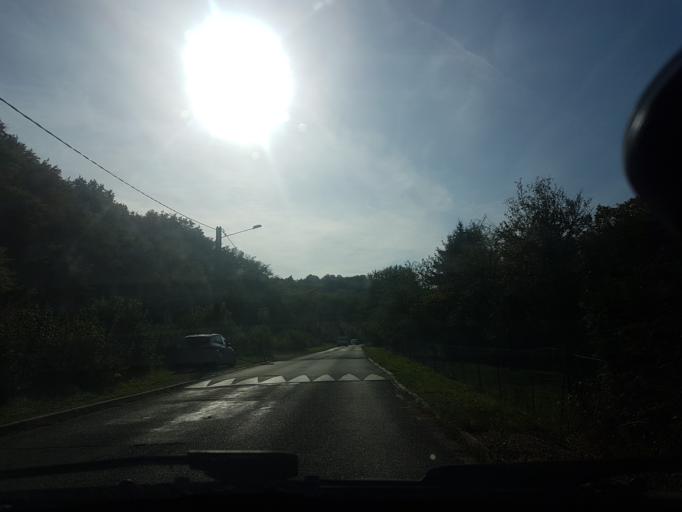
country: FR
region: Franche-Comte
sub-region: Territoire de Belfort
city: Offemont
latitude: 47.6513
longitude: 6.8828
